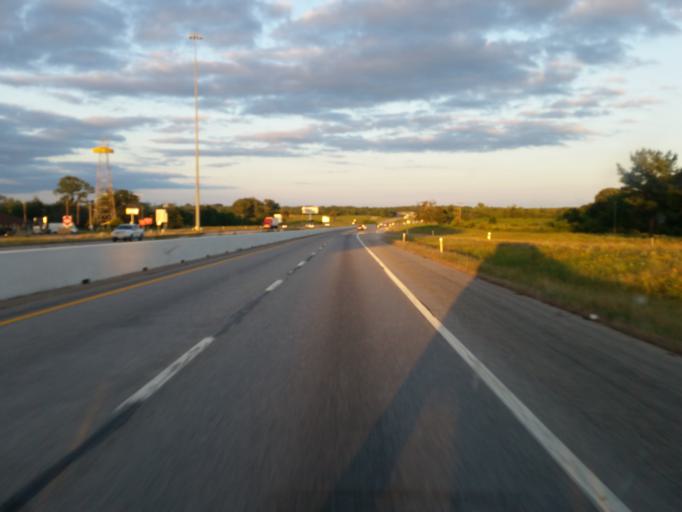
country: US
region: Texas
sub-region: Van Zandt County
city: Van
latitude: 32.5061
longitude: -95.6410
